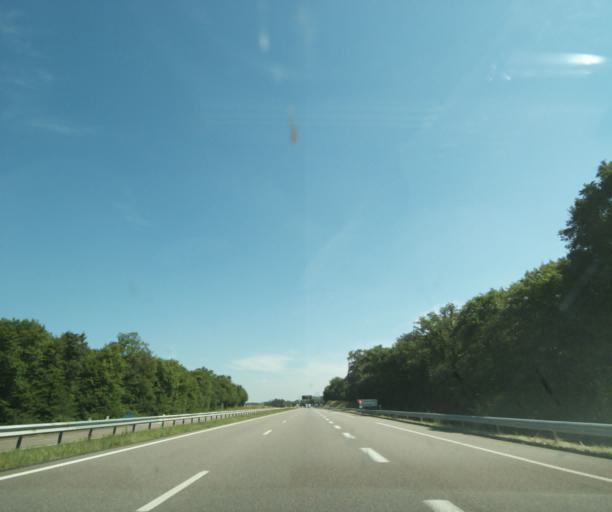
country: FR
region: Lorraine
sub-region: Departement de Meurthe-et-Moselle
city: Colombey-les-Belles
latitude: 48.5116
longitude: 5.9138
